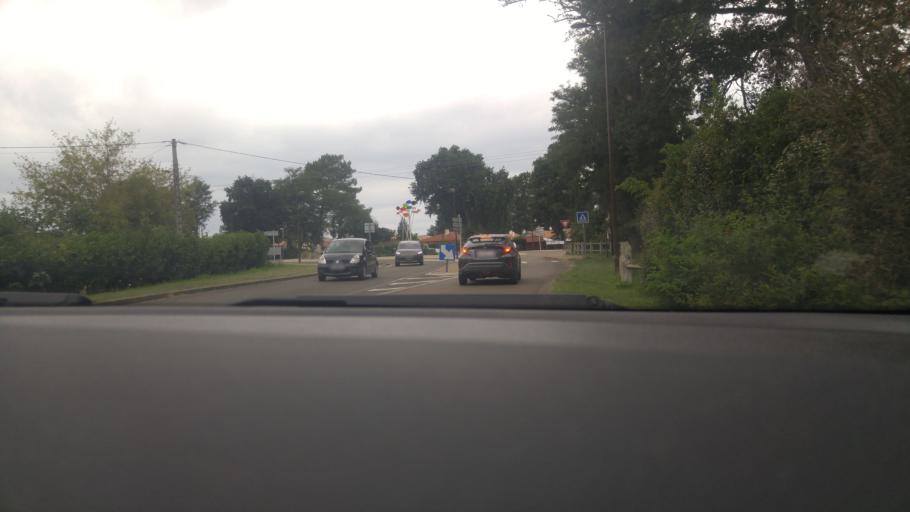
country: FR
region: Aquitaine
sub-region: Departement des Landes
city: Soustons
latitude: 43.7479
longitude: -1.3185
